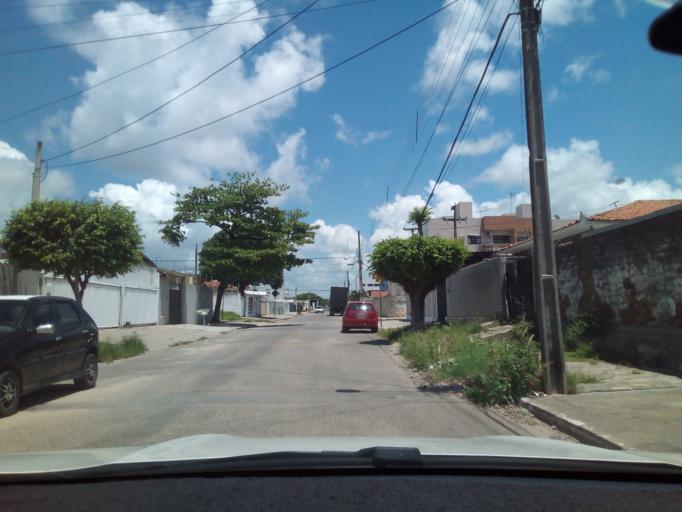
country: BR
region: Paraiba
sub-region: Joao Pessoa
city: Joao Pessoa
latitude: -7.1655
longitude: -34.8683
